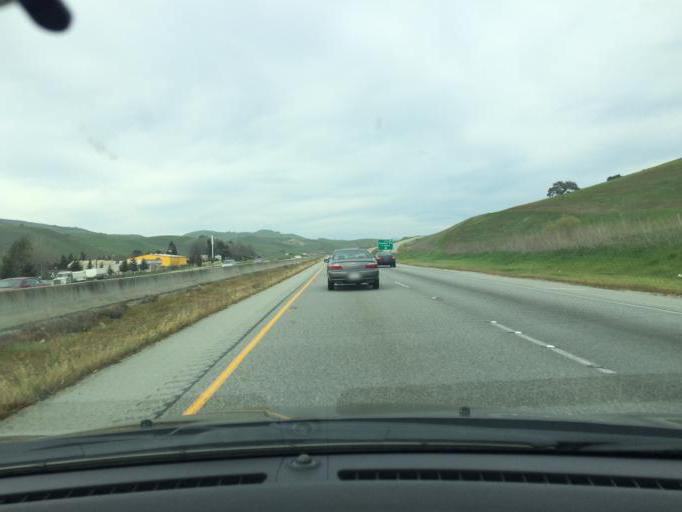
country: US
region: California
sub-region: San Benito County
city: San Juan Bautista
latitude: 36.8973
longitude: -121.5562
